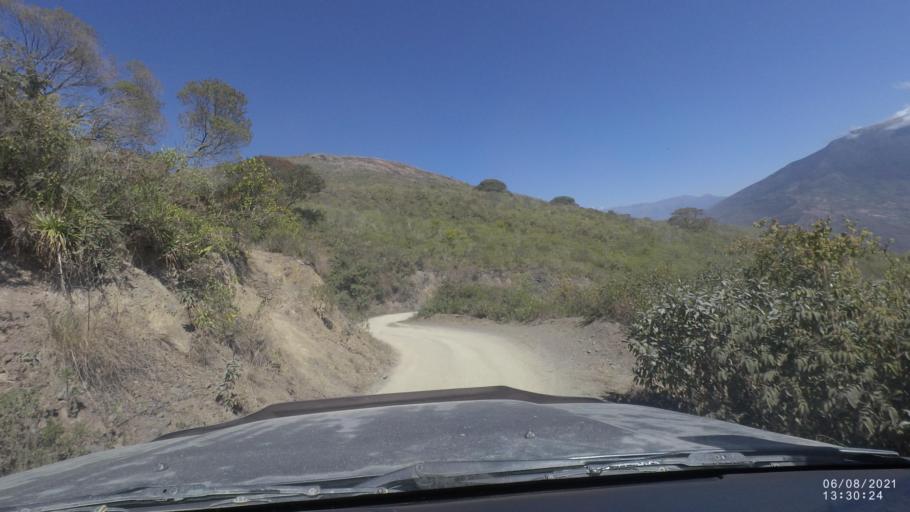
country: BO
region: La Paz
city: Quime
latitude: -16.6998
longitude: -66.7238
